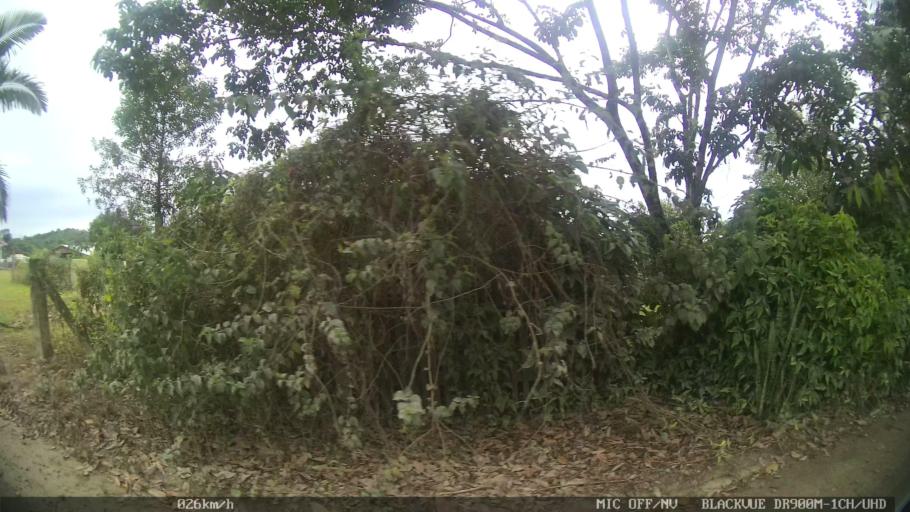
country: BR
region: Santa Catarina
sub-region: Joinville
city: Joinville
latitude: -26.2757
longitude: -48.9366
